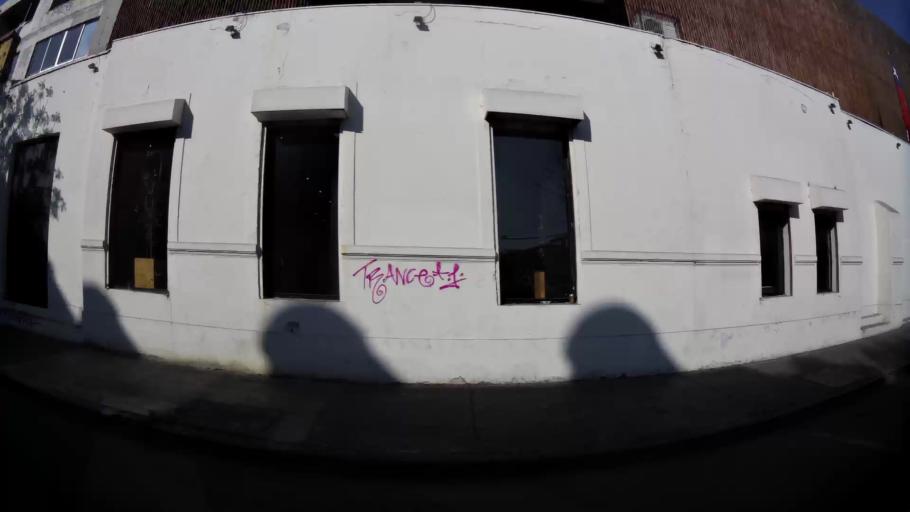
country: CL
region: Santiago Metropolitan
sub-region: Provincia de Santiago
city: Santiago
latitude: -33.4470
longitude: -70.6734
